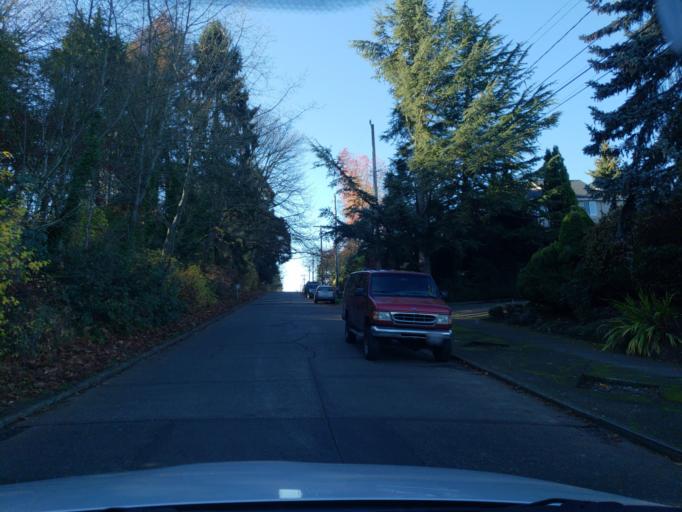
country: US
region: Washington
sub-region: King County
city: Seattle
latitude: 47.6717
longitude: -122.3486
